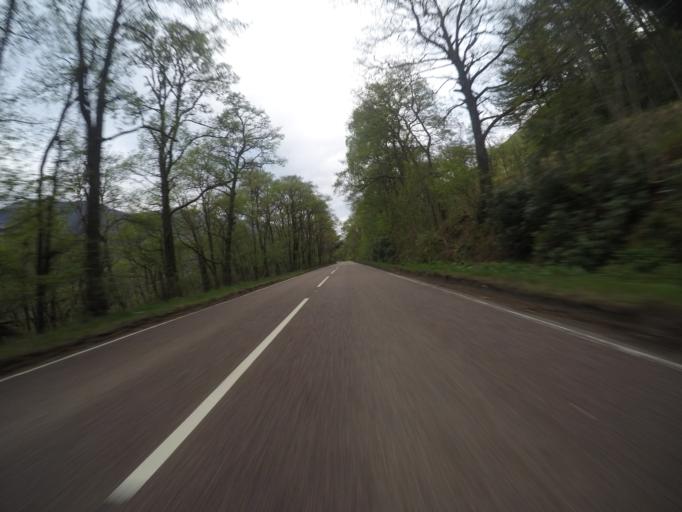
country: GB
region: Scotland
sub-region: Highland
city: Spean Bridge
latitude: 56.9700
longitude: -4.8890
